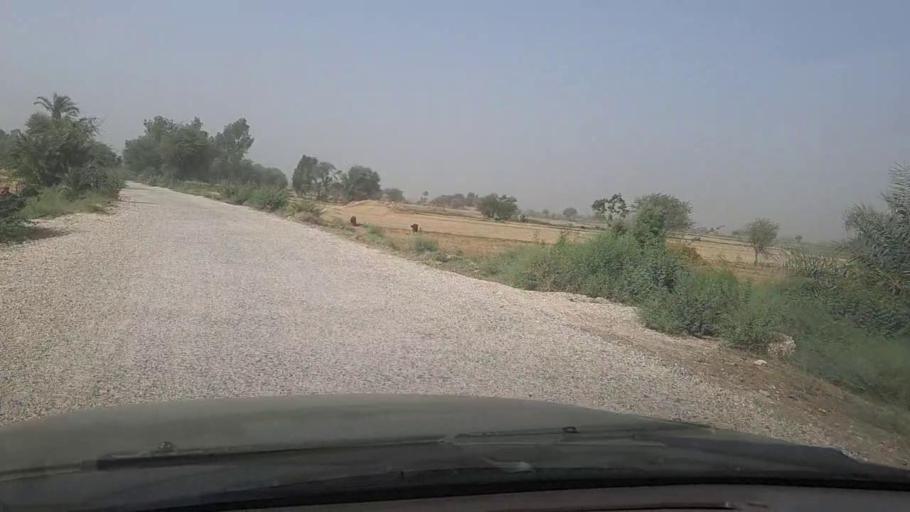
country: PK
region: Sindh
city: Shikarpur
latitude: 27.9135
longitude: 68.6059
